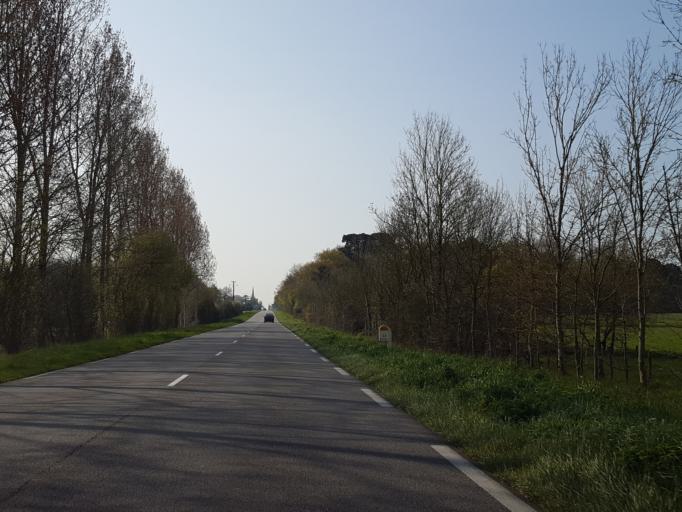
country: FR
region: Pays de la Loire
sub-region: Departement de la Vendee
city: Rocheserviere
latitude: 46.9505
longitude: -1.5127
